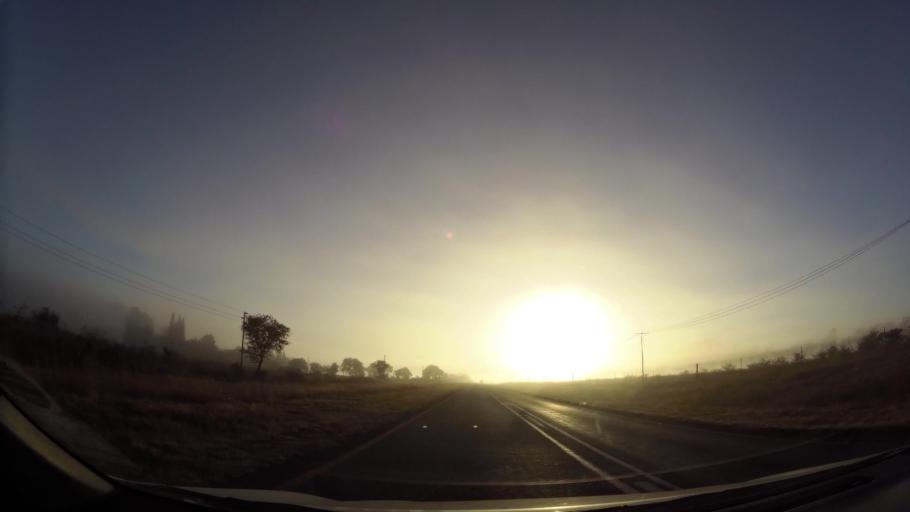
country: ZA
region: Limpopo
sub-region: Capricorn District Municipality
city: Polokwane
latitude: -24.0319
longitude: 29.2874
